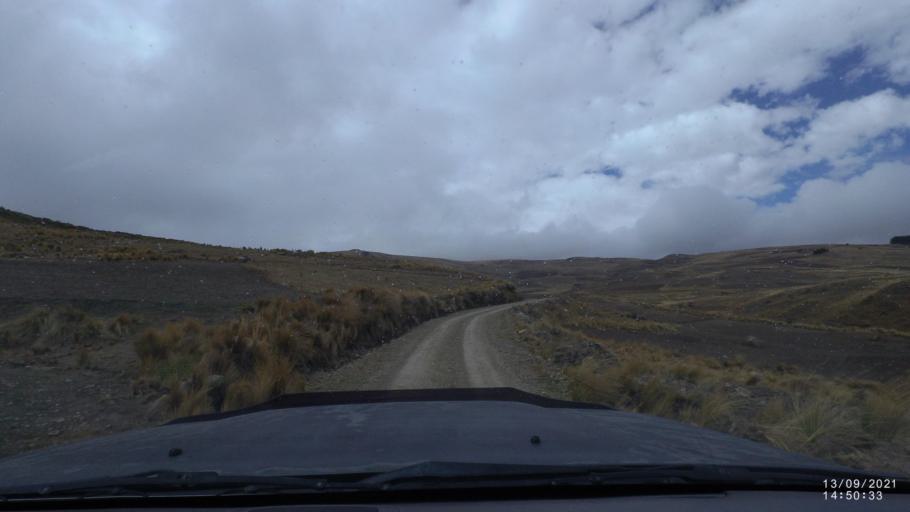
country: BO
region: Cochabamba
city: Colomi
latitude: -17.3470
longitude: -65.7945
